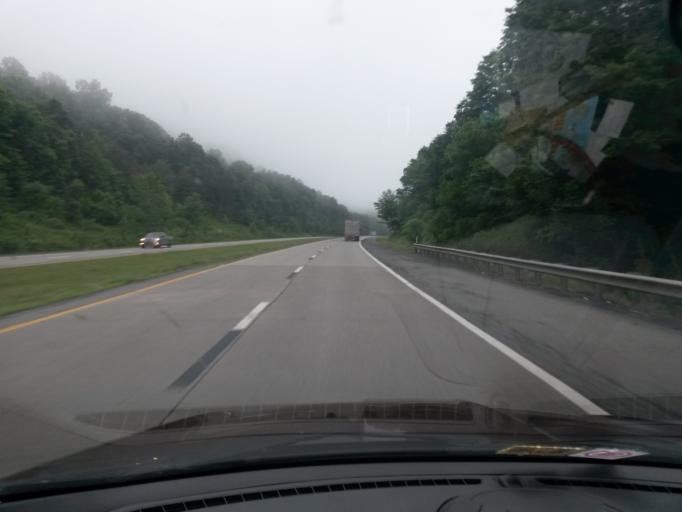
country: US
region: West Virginia
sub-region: Summers County
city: Hinton
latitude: 37.7966
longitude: -80.8474
